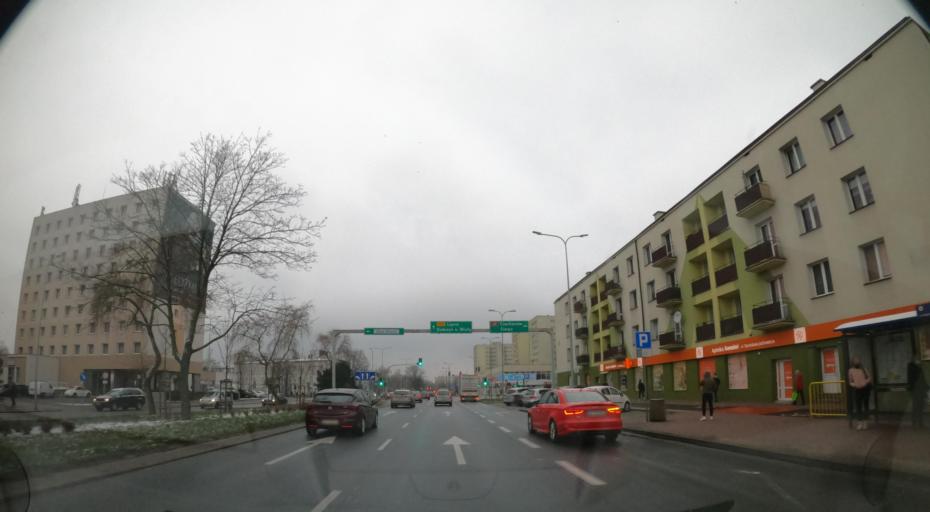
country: PL
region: Masovian Voivodeship
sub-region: Plock
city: Plock
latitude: 52.5496
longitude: 19.6923
